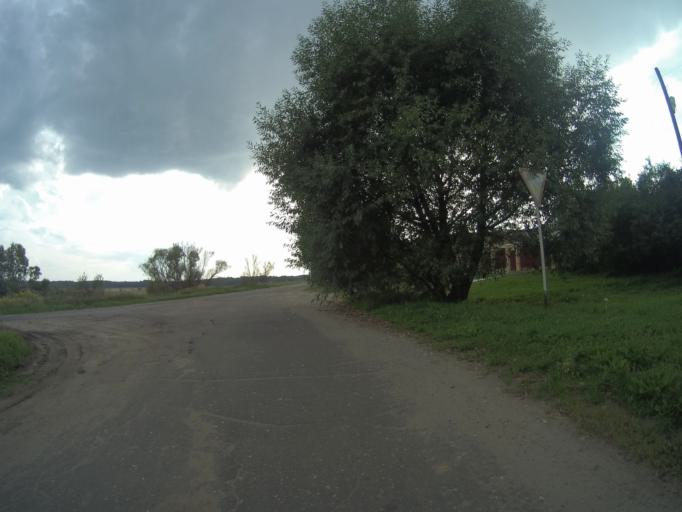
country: RU
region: Vladimir
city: Vorsha
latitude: 56.0127
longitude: 40.1633
